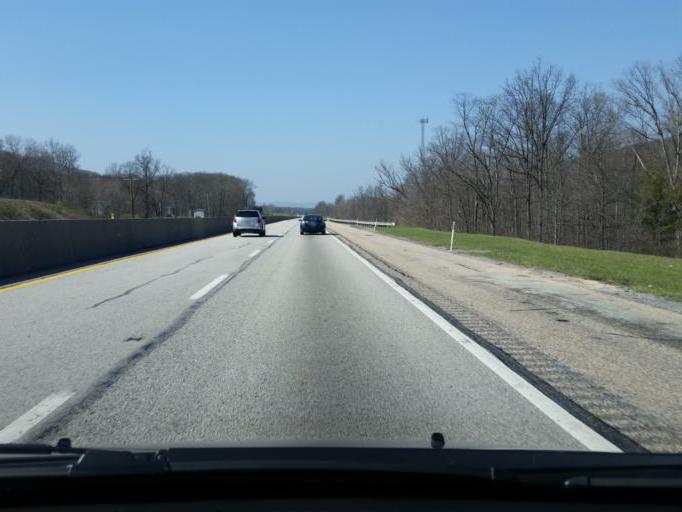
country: US
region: Pennsylvania
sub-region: Franklin County
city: Doylestown
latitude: 40.1460
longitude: -77.7221
